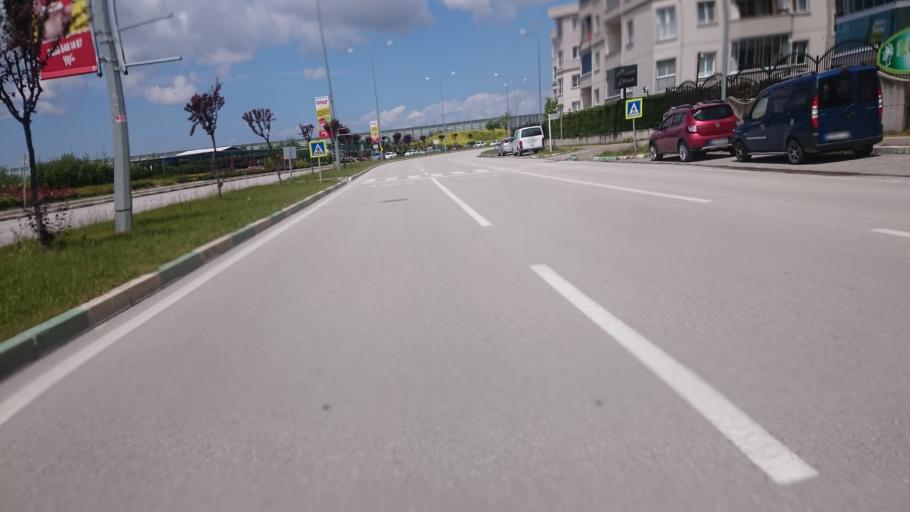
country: TR
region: Bursa
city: Niluefer
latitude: 40.2316
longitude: 28.9163
